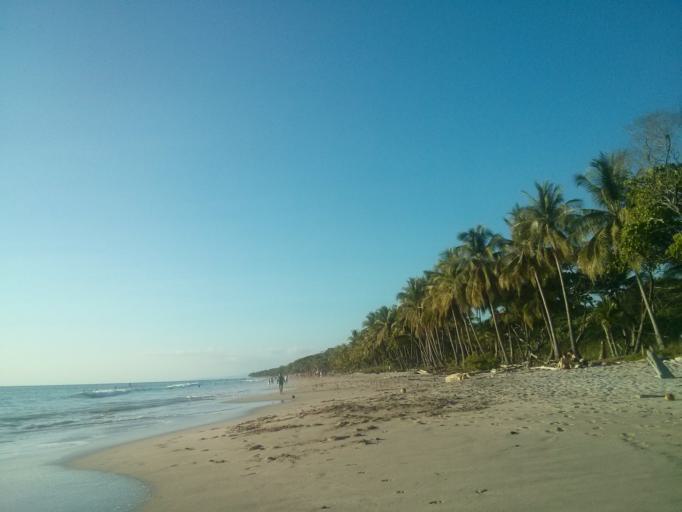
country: CR
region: Guanacaste
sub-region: Canton de Nandayure
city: Bejuco
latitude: 9.6247
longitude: -85.1503
